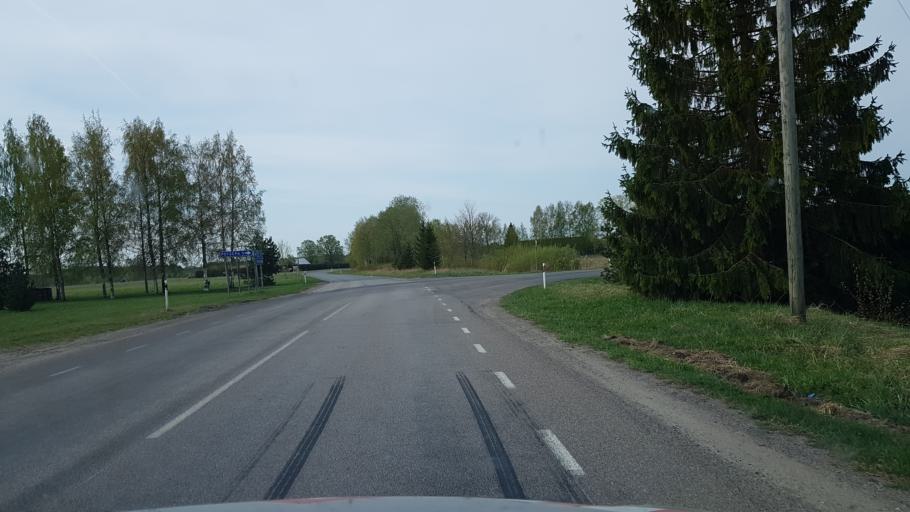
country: EE
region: Paernumaa
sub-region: Audru vald
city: Audru
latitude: 58.3657
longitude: 24.2639
